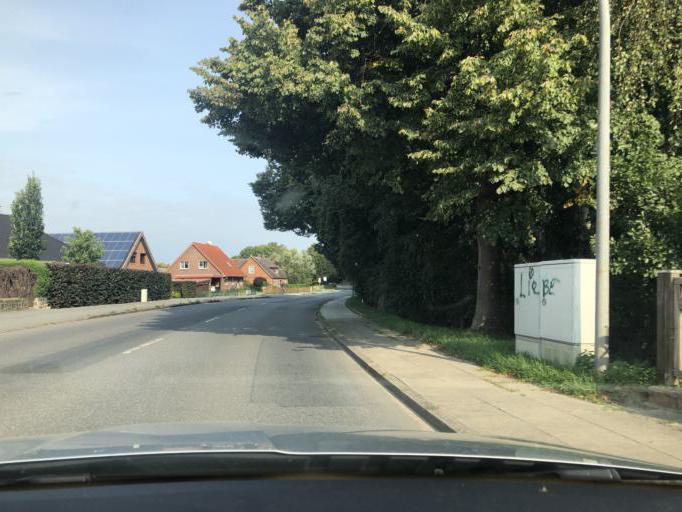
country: DE
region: Schleswig-Holstein
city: Gross Gronau
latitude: 53.8069
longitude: 10.7490
